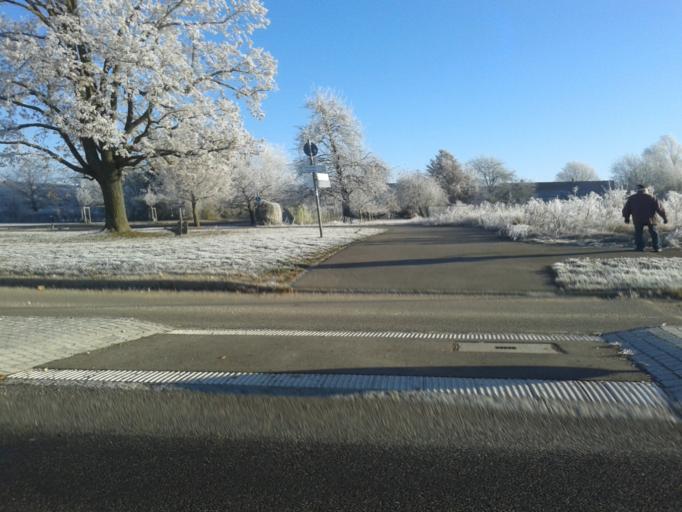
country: DE
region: Baden-Wuerttemberg
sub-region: Tuebingen Region
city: Dornstadt
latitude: 48.4309
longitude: 9.9630
